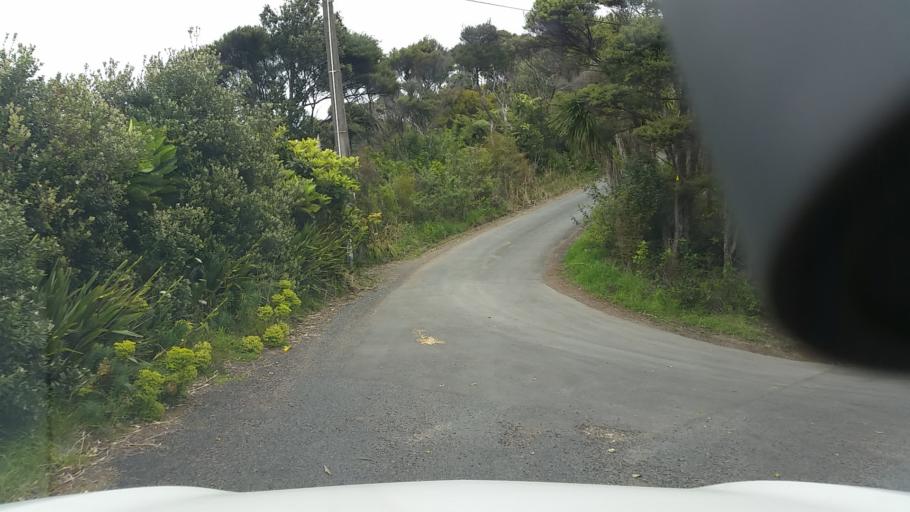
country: NZ
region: Auckland
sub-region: Auckland
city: Muriwai Beach
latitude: -36.8767
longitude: 174.4662
